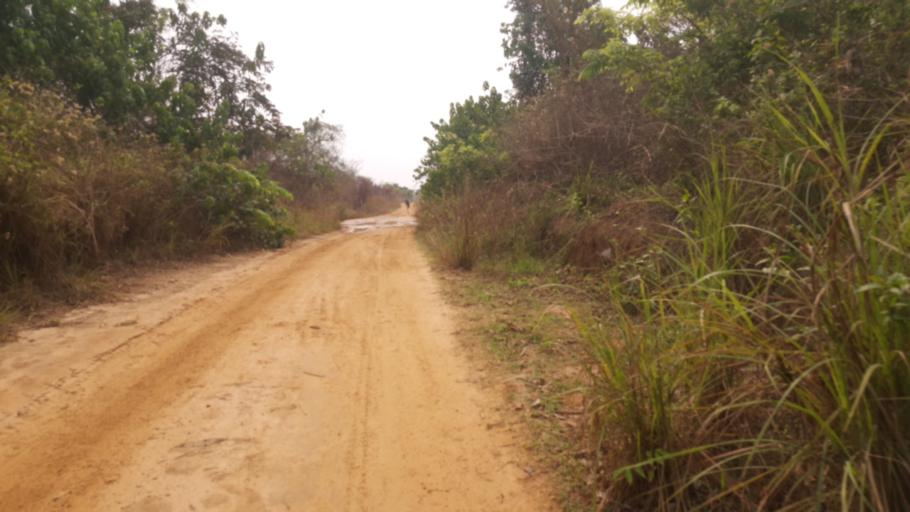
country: CD
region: Bandundu
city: Bandundu
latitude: -3.4549
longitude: 17.7456
